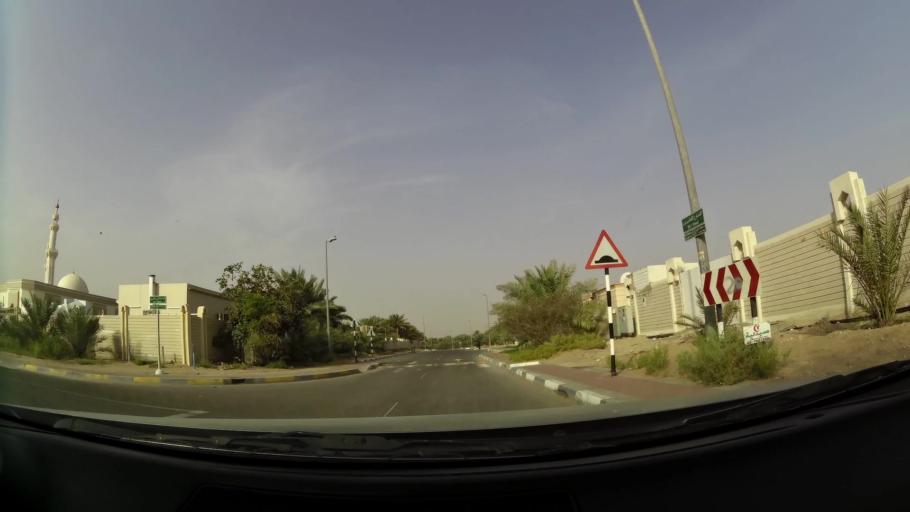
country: AE
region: Abu Dhabi
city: Al Ain
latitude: 24.1307
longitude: 55.6858
